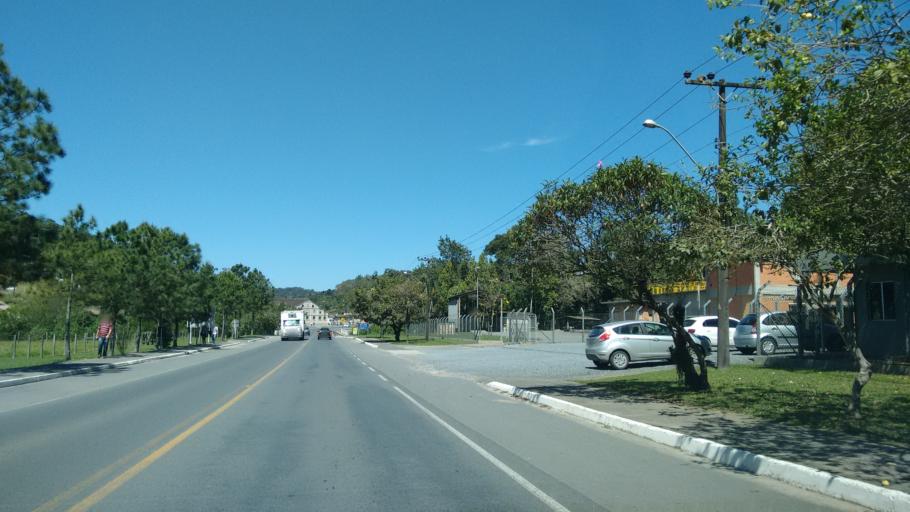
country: BR
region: Santa Catarina
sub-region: Indaial
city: Indaial
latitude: -26.8497
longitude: -49.1526
